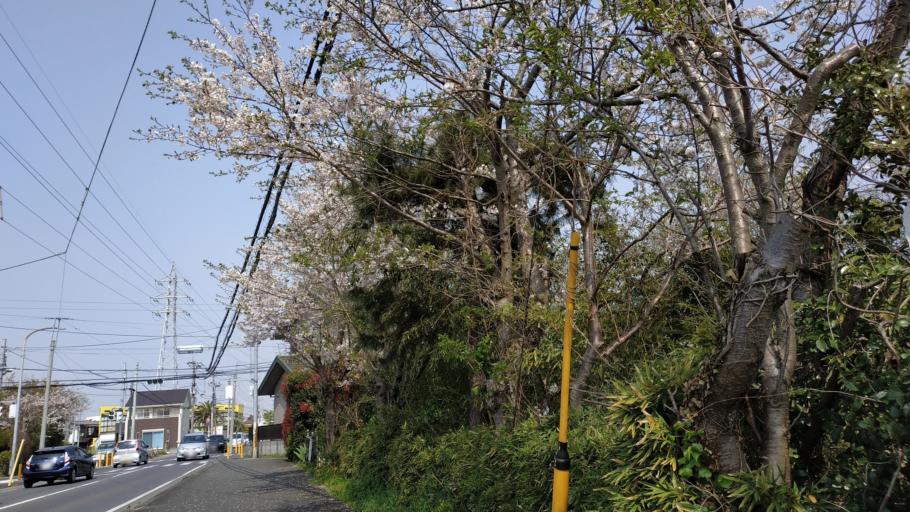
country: JP
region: Chiba
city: Ichihara
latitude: 35.5068
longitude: 140.0903
